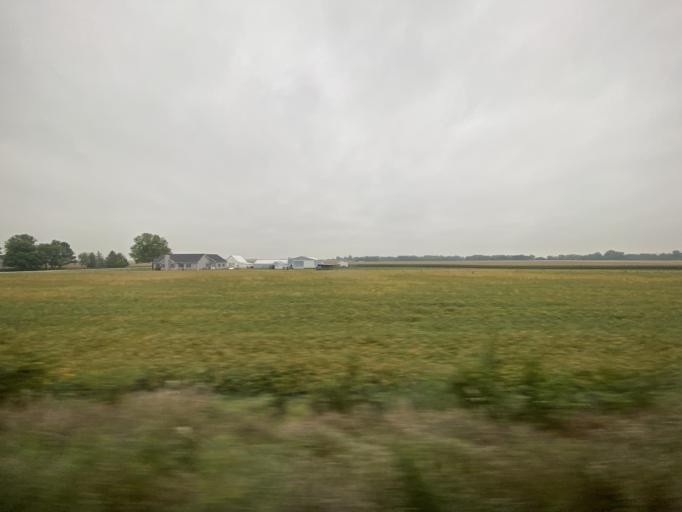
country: US
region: Illinois
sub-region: DeKalb County
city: Somonauk
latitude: 41.6217
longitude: -88.7530
